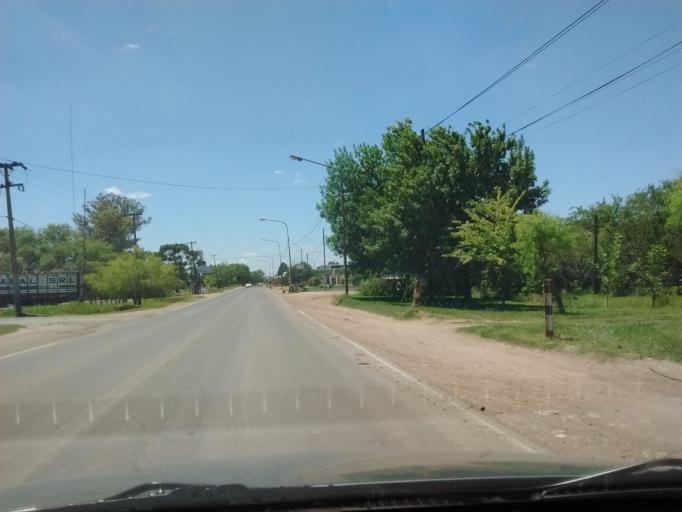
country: AR
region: Entre Rios
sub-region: Departamento de Gualeguay
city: Gualeguay
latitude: -33.1260
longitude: -59.3248
